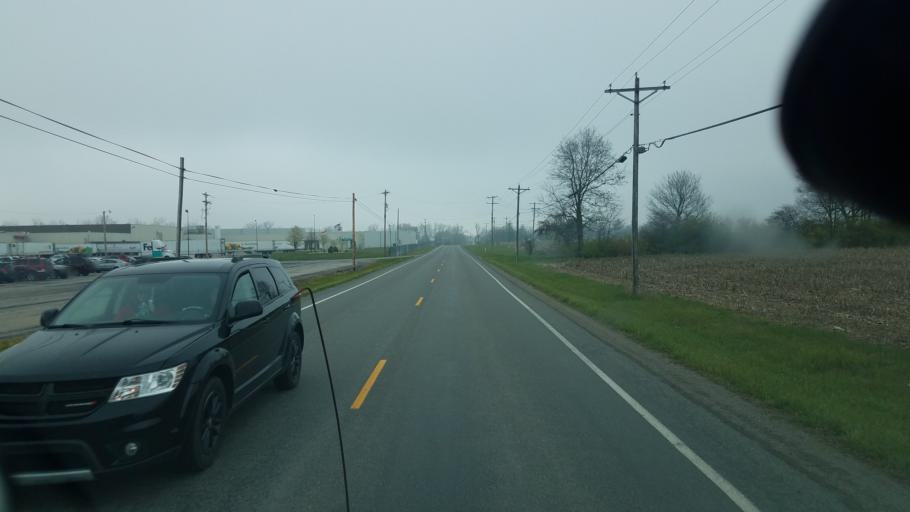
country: US
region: Ohio
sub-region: Logan County
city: Bellefontaine
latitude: 40.4072
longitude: -83.7995
